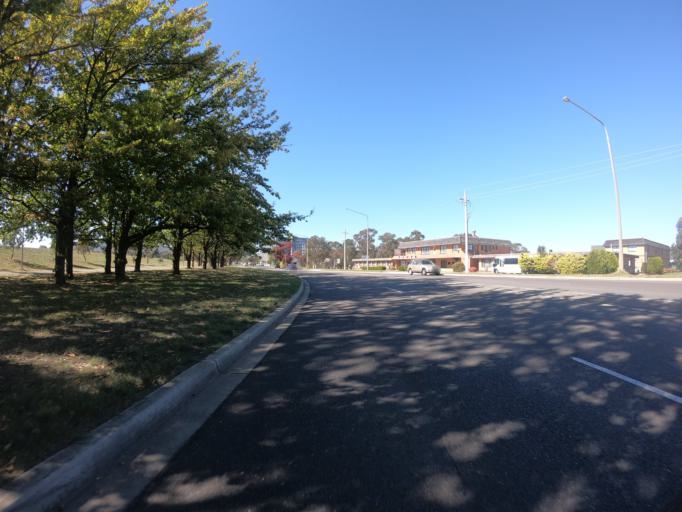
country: AU
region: Australian Capital Territory
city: Acton
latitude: -35.2477
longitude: 149.1286
